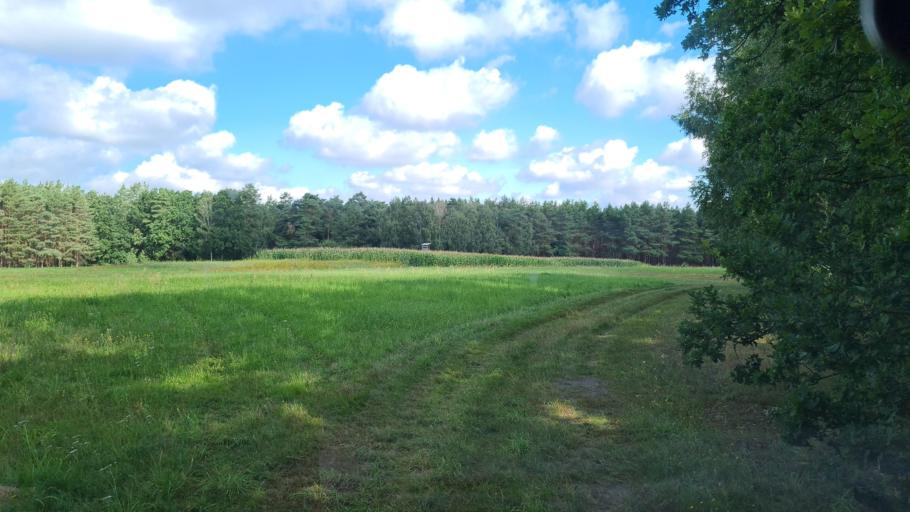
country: DE
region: Brandenburg
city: Sonnewalde
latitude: 51.7409
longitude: 13.6947
